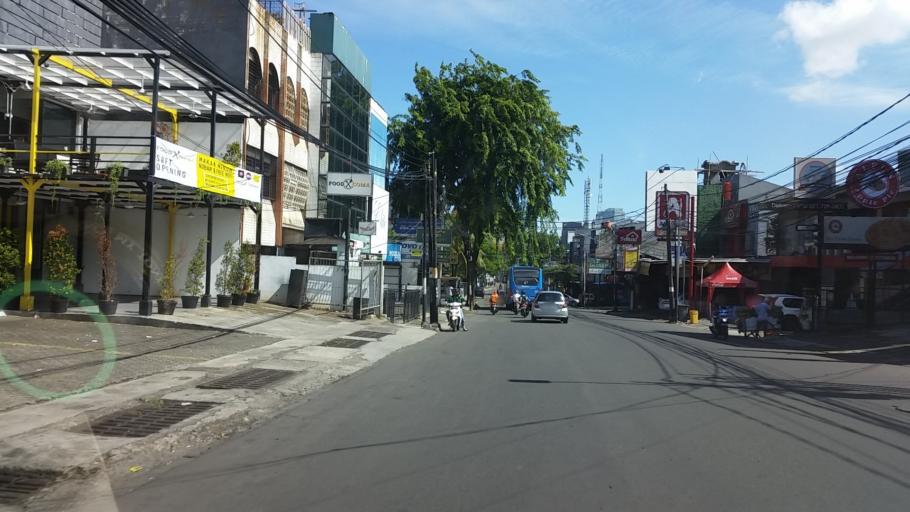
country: ID
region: Jakarta Raya
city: Jakarta
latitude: -6.2590
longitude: 106.7893
